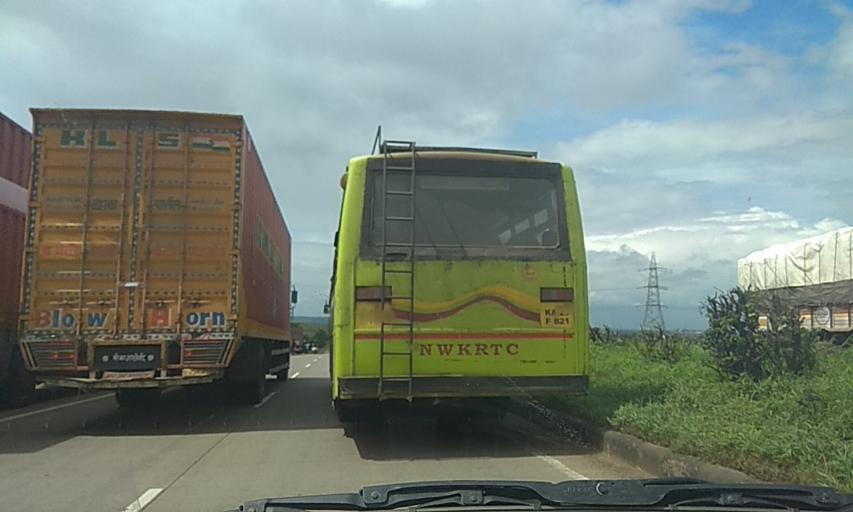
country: IN
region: Maharashtra
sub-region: Kolhapur
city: Kagal
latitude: 16.5158
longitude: 74.3276
